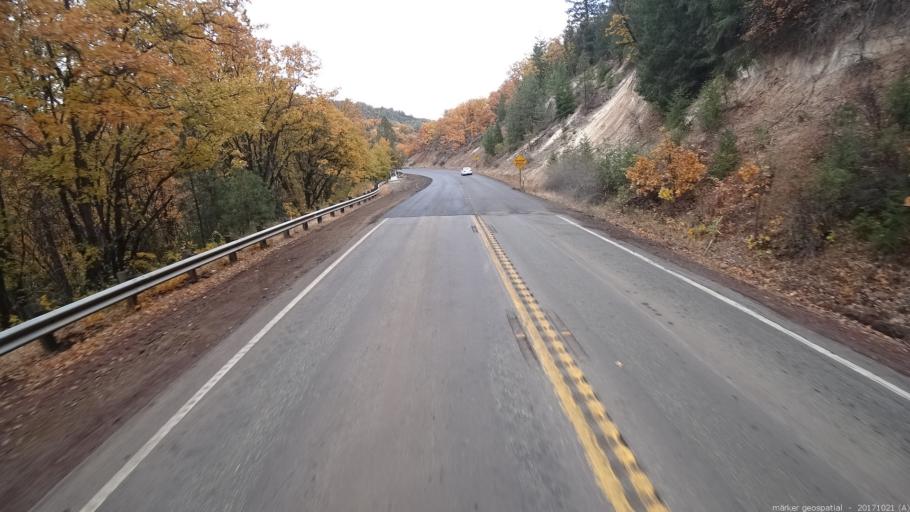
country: US
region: California
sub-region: Shasta County
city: Burney
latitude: 41.0158
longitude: -121.6246
